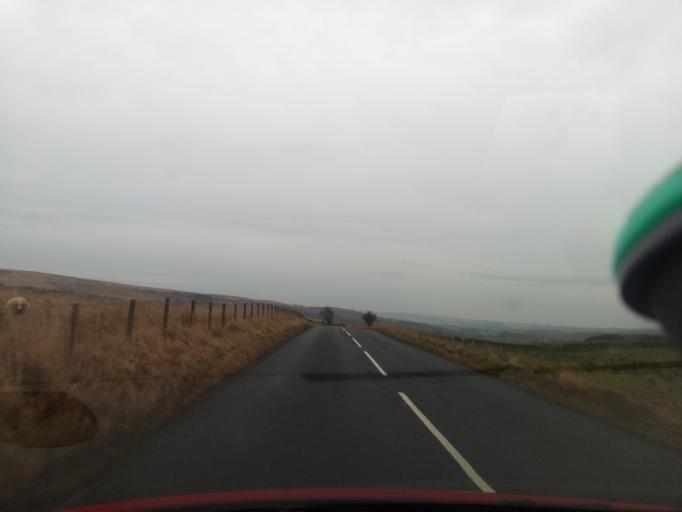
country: GB
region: England
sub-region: Northumberland
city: Rochester
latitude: 55.1646
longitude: -2.3229
